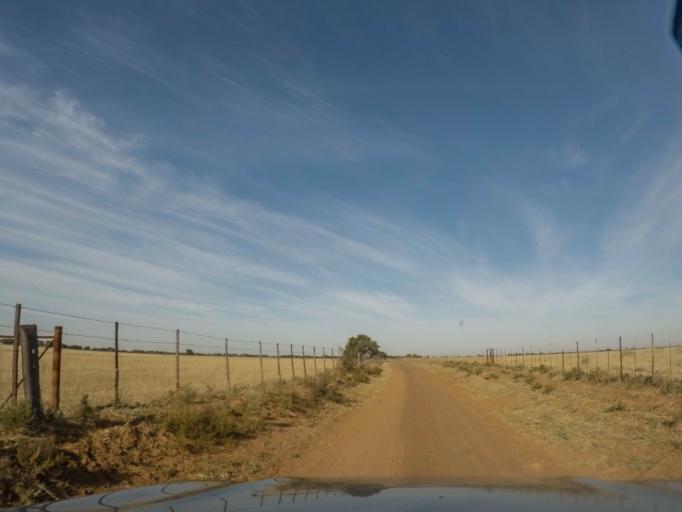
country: BW
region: South East
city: Janeng
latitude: -25.6457
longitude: 25.2580
